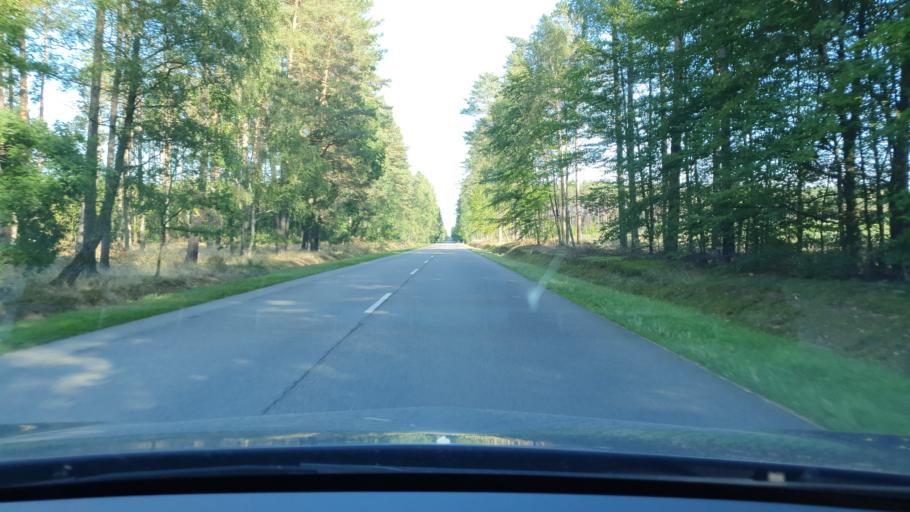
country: PL
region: West Pomeranian Voivodeship
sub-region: Powiat kamienski
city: Golczewo
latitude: 53.8140
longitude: 15.0736
